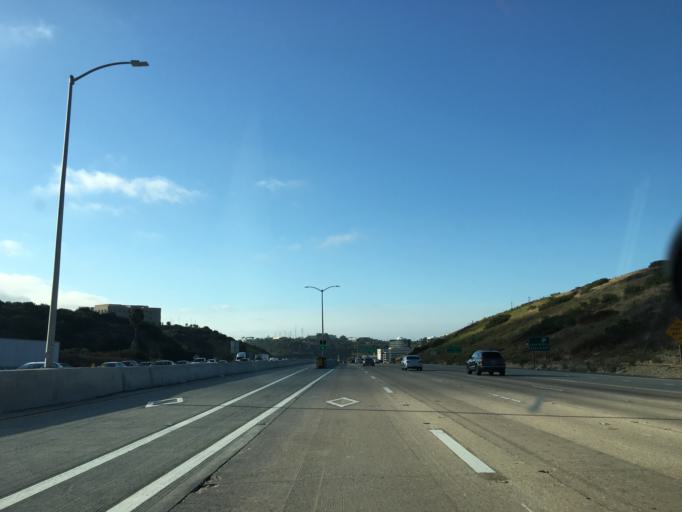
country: US
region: California
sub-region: San Diego County
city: La Jolla
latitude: 32.8811
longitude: -117.2013
